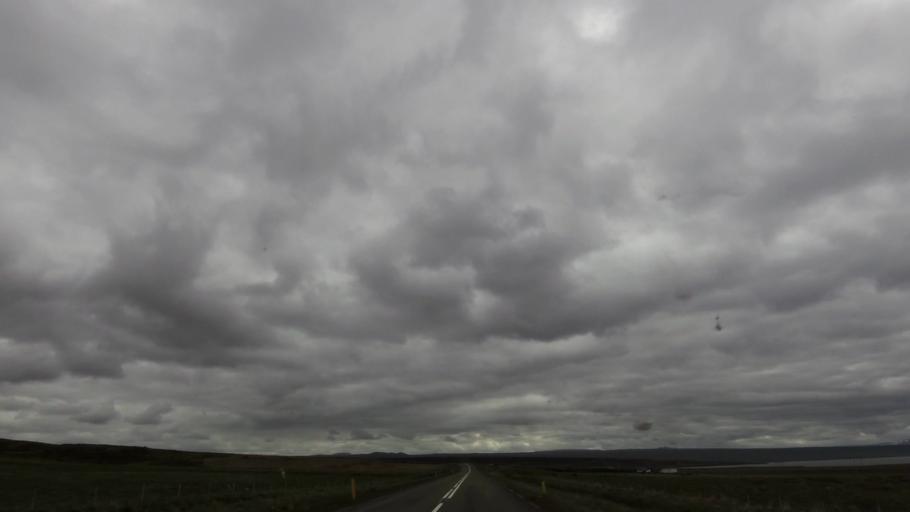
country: IS
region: West
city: Borgarnes
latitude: 65.2239
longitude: -21.7526
